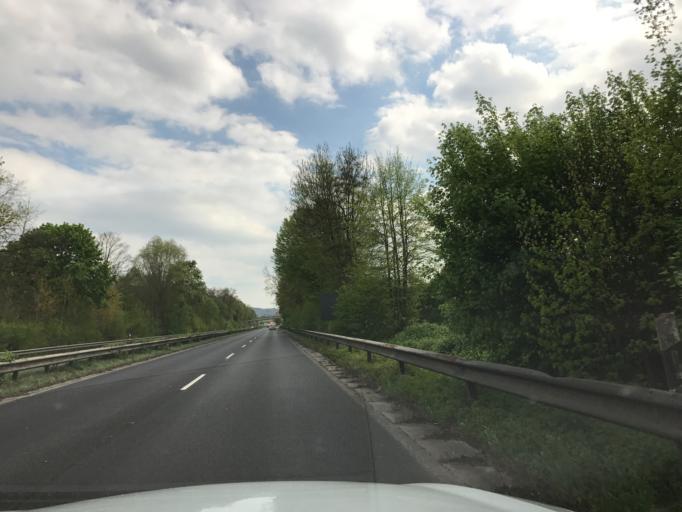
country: DE
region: North Rhine-Westphalia
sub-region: Regierungsbezirk Koln
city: Bad Honnef
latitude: 50.6474
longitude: 7.2167
